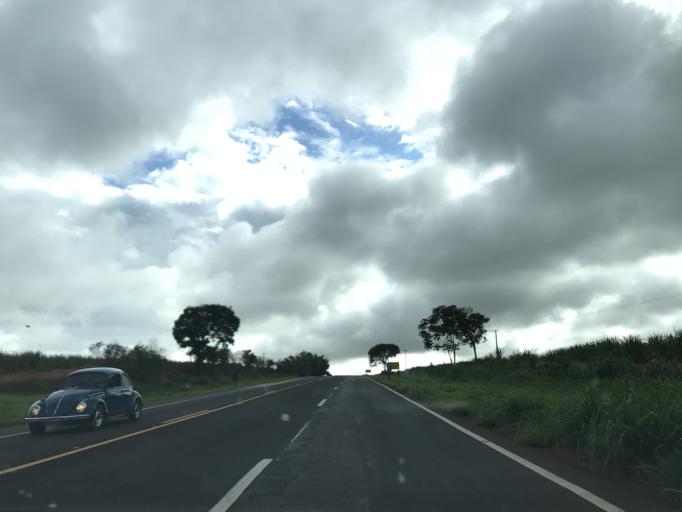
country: BR
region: Sao Paulo
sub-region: Penapolis
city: Penapolis
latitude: -21.4956
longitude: -50.2413
